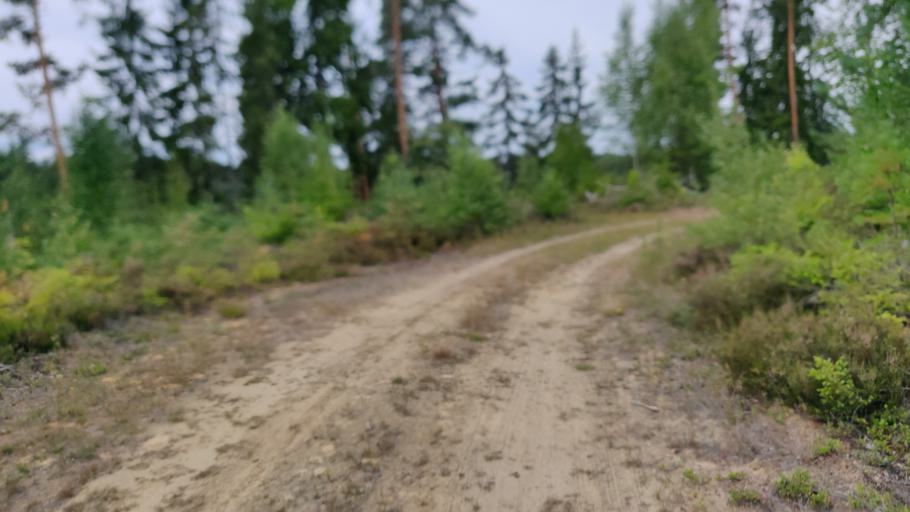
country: SE
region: Vaermland
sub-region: Hagfors Kommun
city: Hagfors
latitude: 60.0185
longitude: 13.5434
